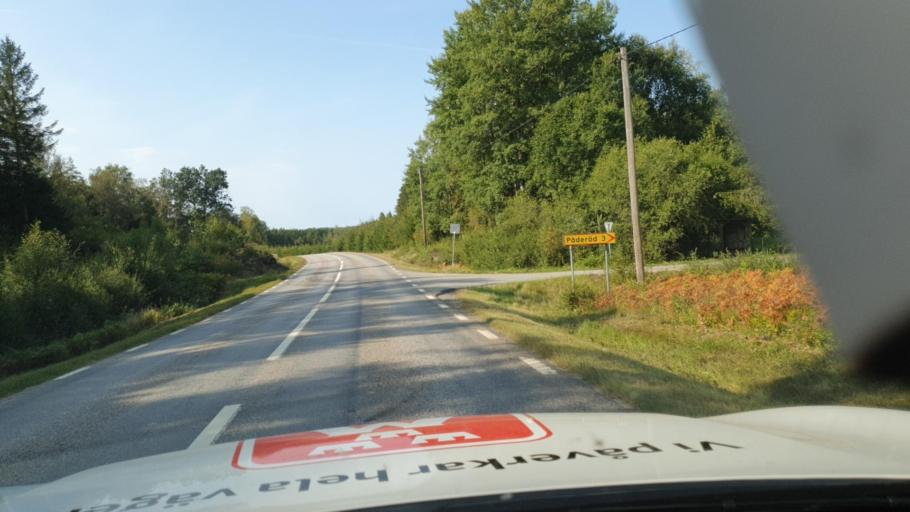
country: SE
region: Vaestra Goetaland
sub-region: Tanums Kommun
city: Tanumshede
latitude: 58.7499
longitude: 11.5166
